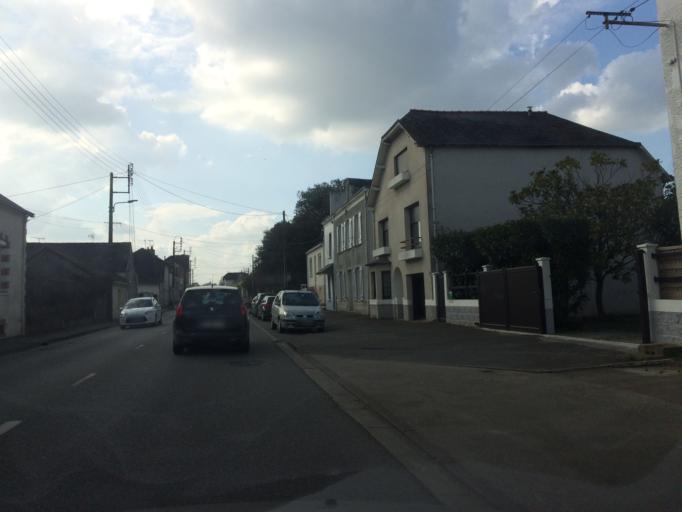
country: FR
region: Pays de la Loire
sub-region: Departement de la Loire-Atlantique
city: Blain
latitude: 47.4772
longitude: -1.7677
